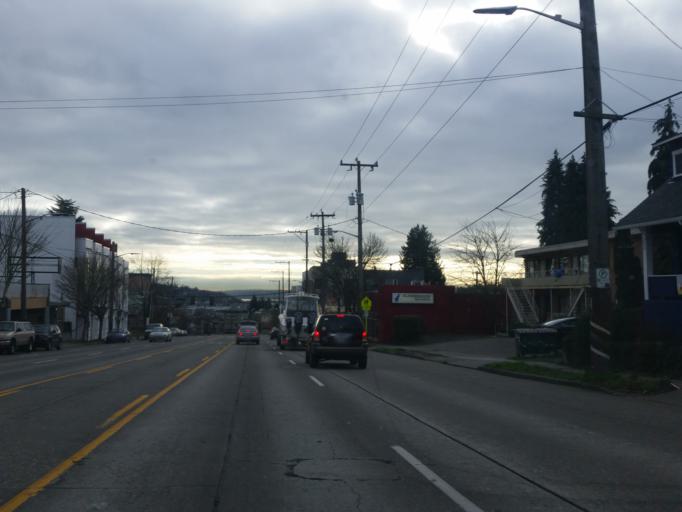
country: US
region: Washington
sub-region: King County
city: Shoreline
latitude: 47.6789
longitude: -122.3768
